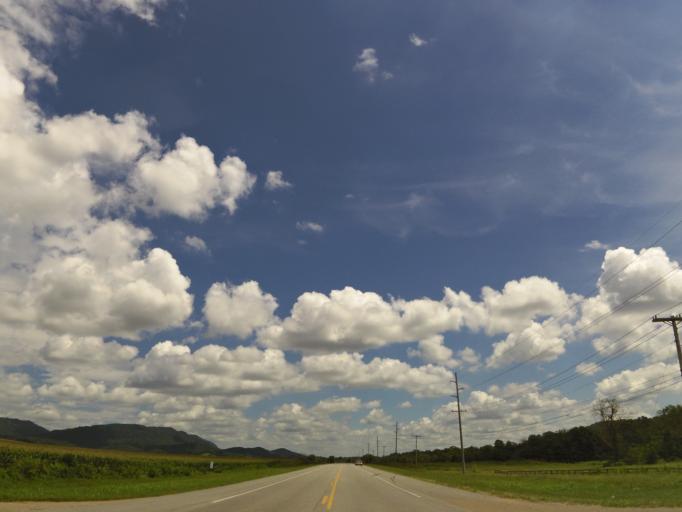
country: US
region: Kentucky
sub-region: Bell County
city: Middlesboro
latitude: 36.5182
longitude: -83.7642
